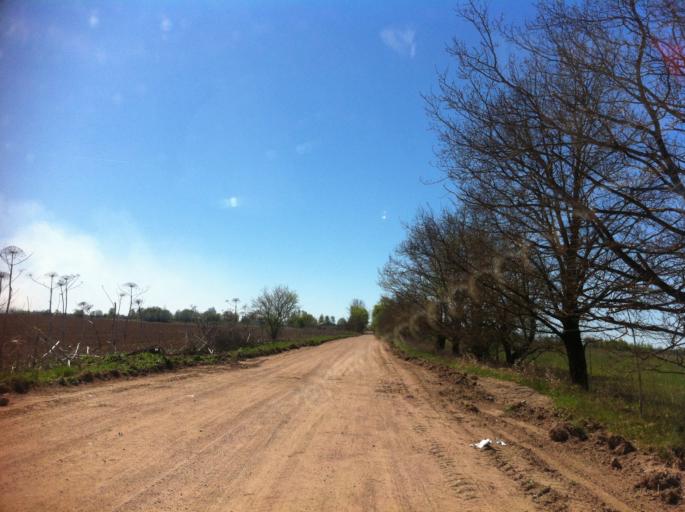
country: RU
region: Pskov
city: Izborsk
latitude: 57.7955
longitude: 27.9638
